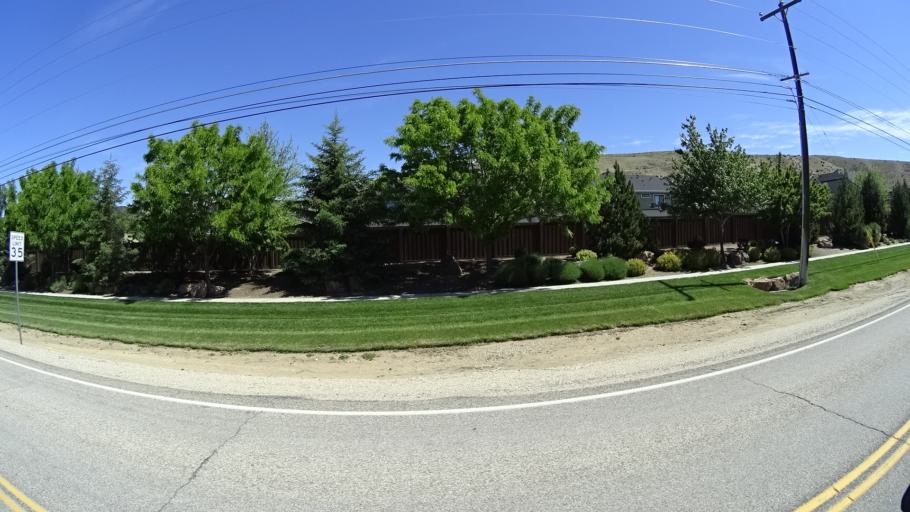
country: US
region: Idaho
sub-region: Ada County
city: Boise
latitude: 43.5637
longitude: -116.1101
